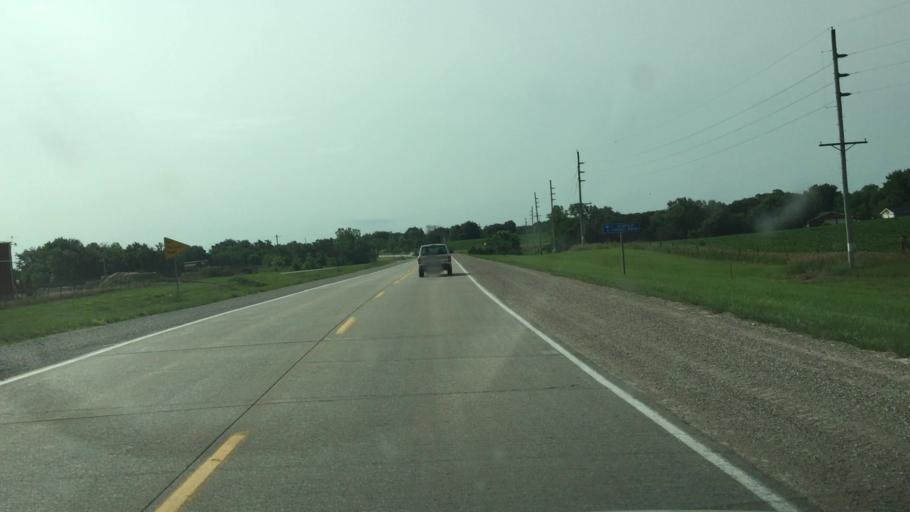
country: US
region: Illinois
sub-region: Hancock County
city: Nauvoo
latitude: 40.6367
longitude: -91.5190
